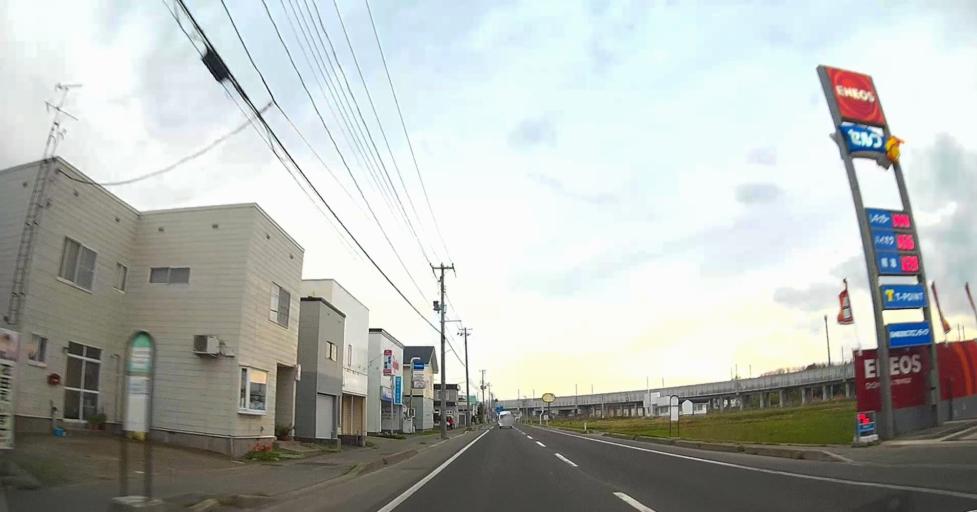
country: JP
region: Aomori
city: Aomori Shi
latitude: 40.8559
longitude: 140.6814
